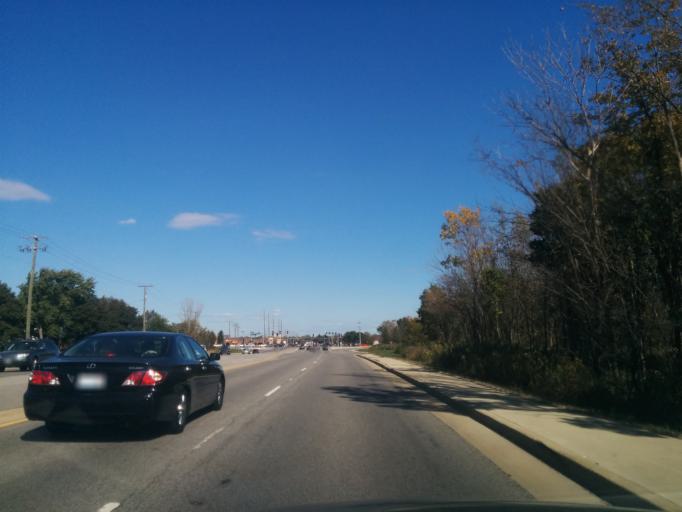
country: US
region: Illinois
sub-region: DuPage County
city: Wheaton
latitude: 41.8264
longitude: -88.1067
